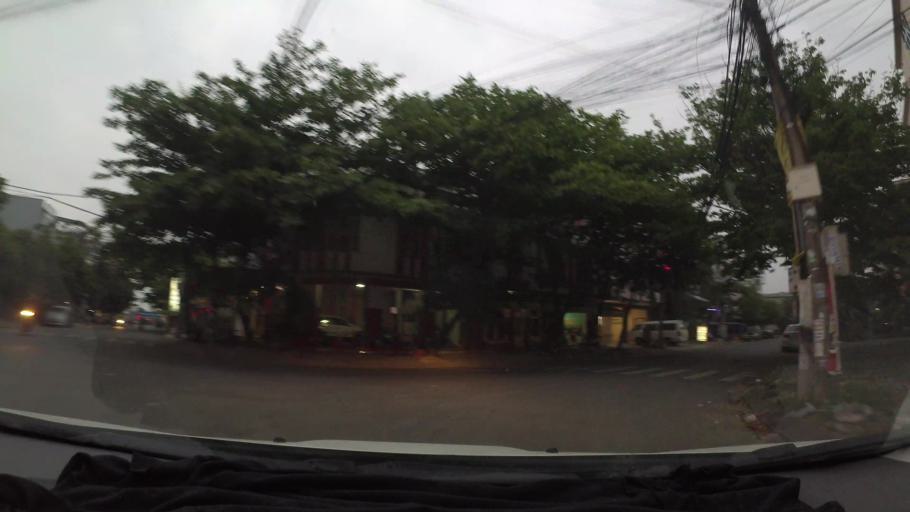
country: VN
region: Da Nang
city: Lien Chieu
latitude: 16.0546
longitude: 108.1714
